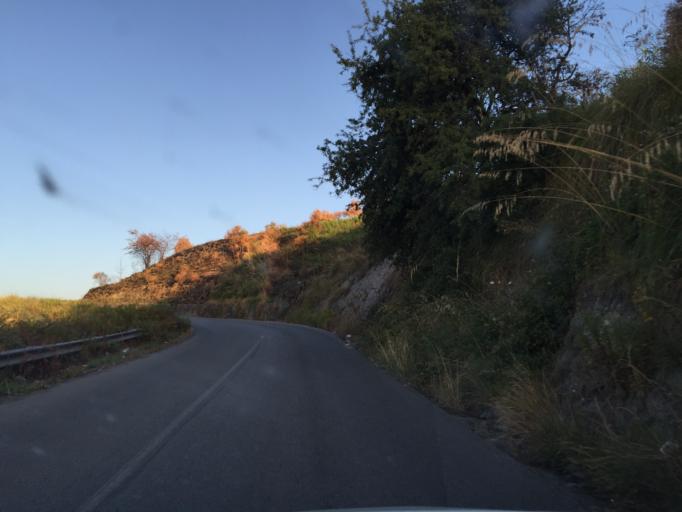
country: IT
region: Calabria
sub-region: Provincia di Vibo-Valentia
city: Briatico
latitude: 38.7165
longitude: 16.0485
